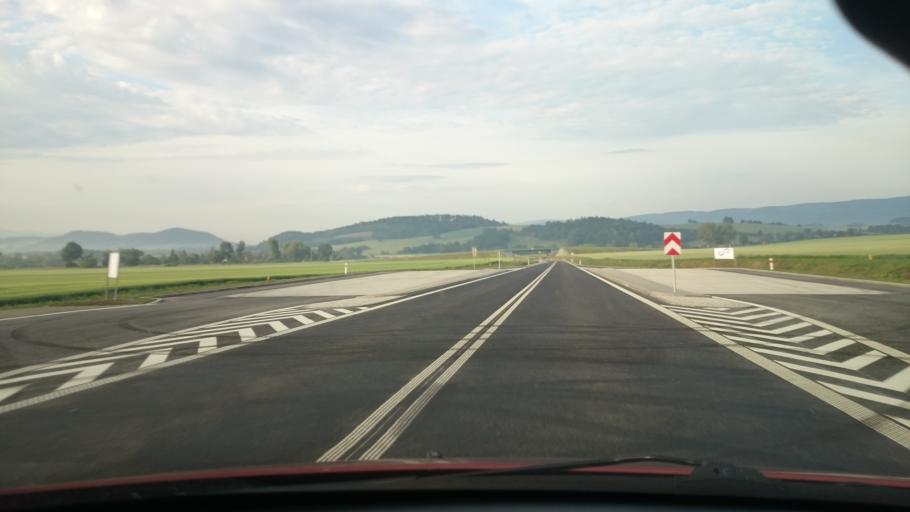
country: PL
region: Lower Silesian Voivodeship
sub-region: Powiat klodzki
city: Klodzko
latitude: 50.4244
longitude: 16.6273
